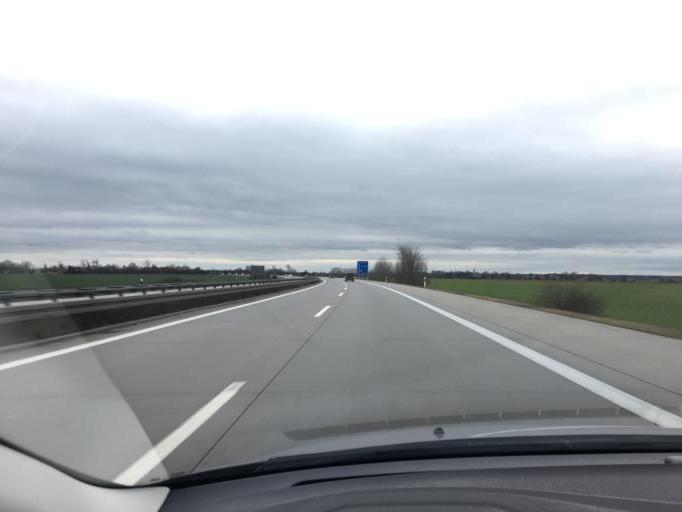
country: DE
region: Saxony
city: Borsdorf
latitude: 51.3263
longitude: 12.5144
